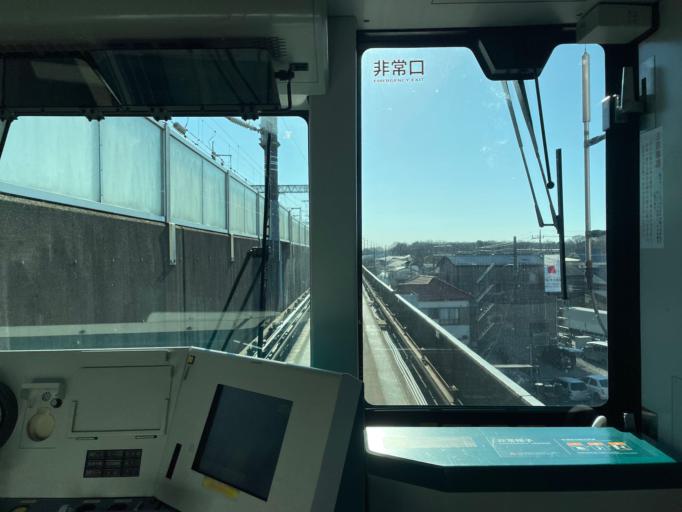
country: JP
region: Saitama
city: Ageoshimo
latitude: 35.9950
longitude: 139.6204
